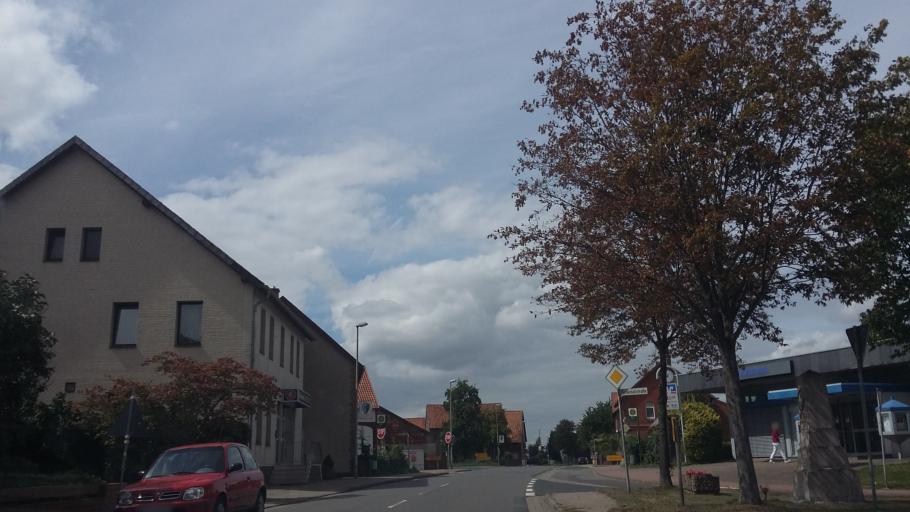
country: DE
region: Lower Saxony
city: Harsum
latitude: 52.2057
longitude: 10.0061
